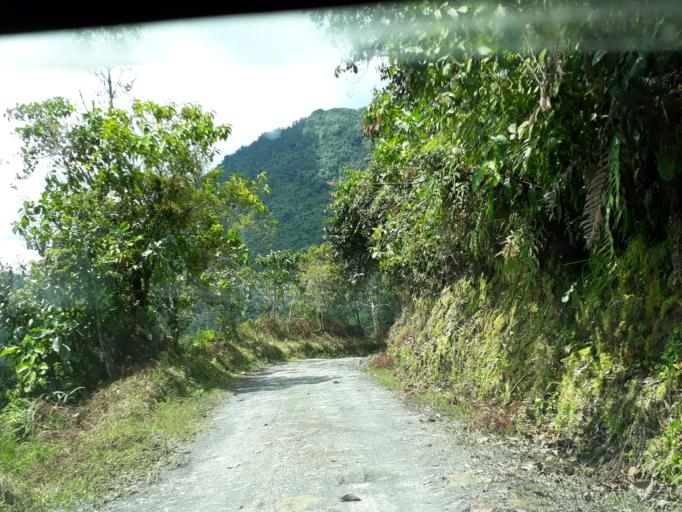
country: CO
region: Cundinamarca
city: Topaipi
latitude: 5.3162
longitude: -74.2121
